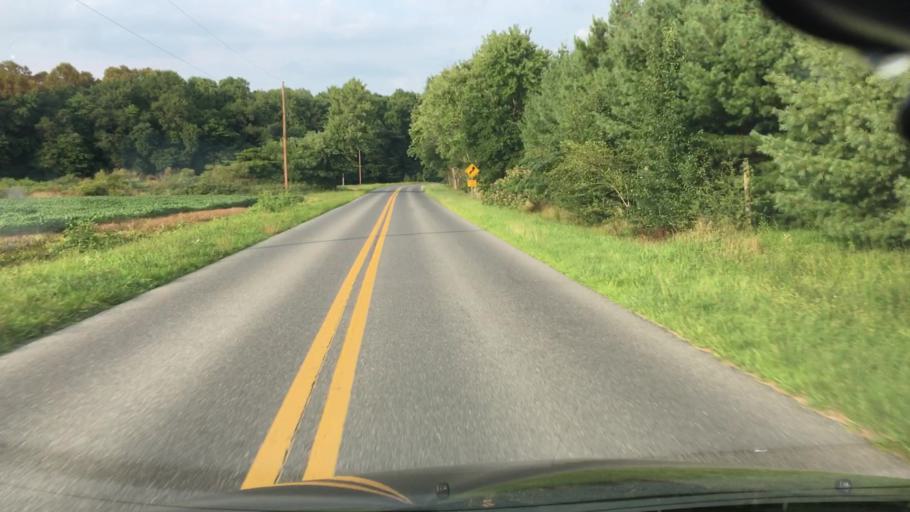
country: US
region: Delaware
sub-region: Sussex County
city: Selbyville
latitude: 38.4677
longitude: -75.1509
